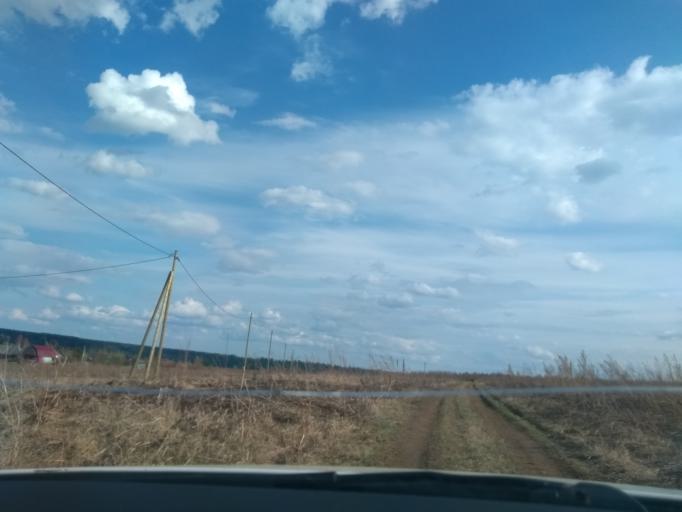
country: RU
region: Perm
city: Sylva
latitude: 57.8432
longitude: 56.7900
